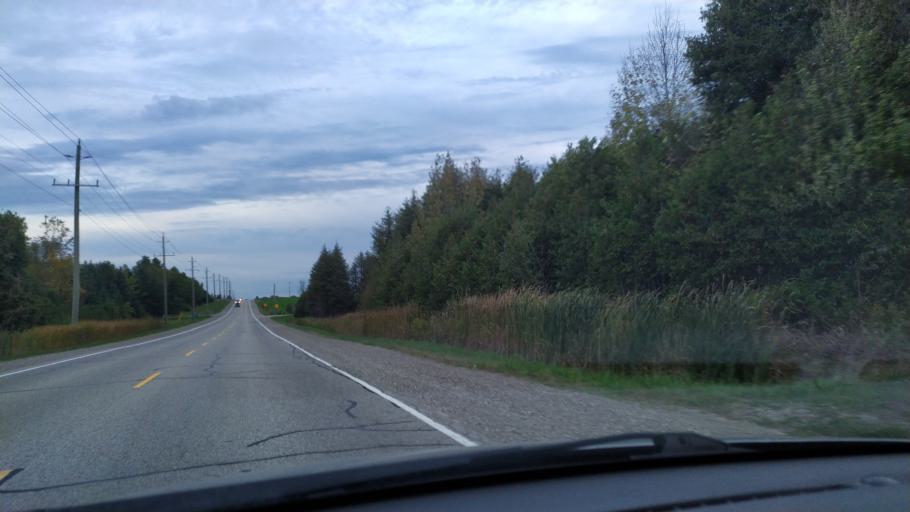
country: CA
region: Ontario
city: Stratford
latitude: 43.4913
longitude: -80.7712
